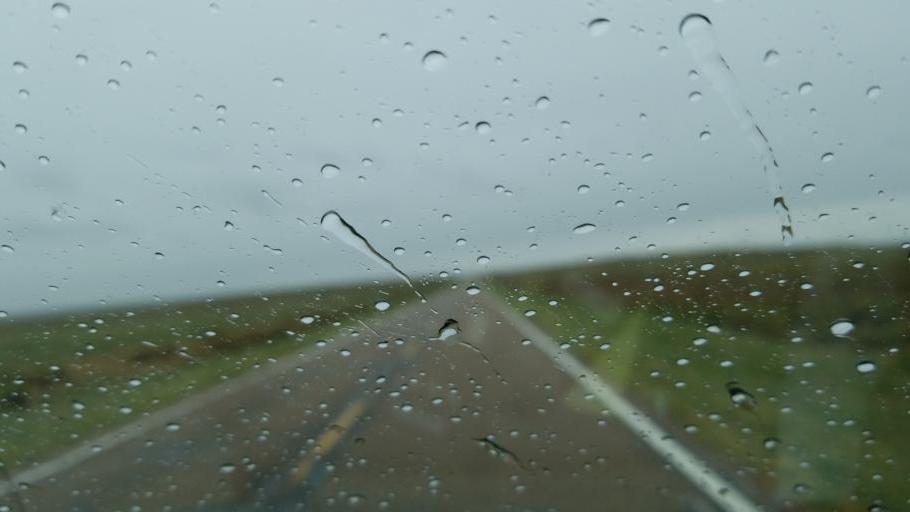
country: US
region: Colorado
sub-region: Lincoln County
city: Hugo
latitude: 38.8560
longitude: -103.1516
